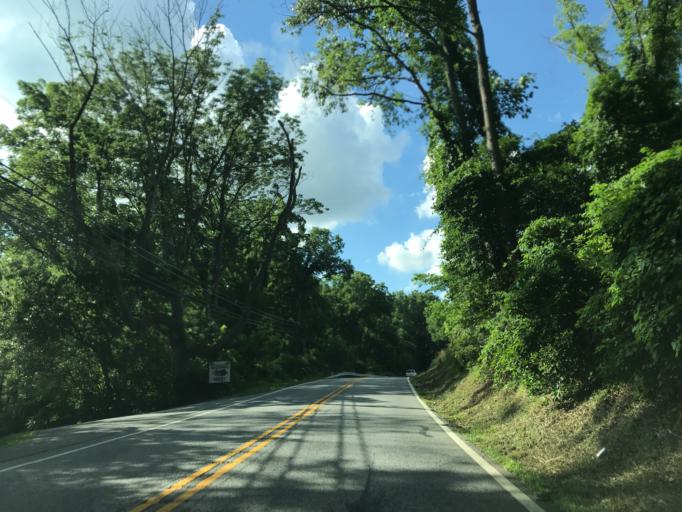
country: US
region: Maryland
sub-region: Carroll County
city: Hampstead
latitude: 39.5565
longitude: -76.7456
